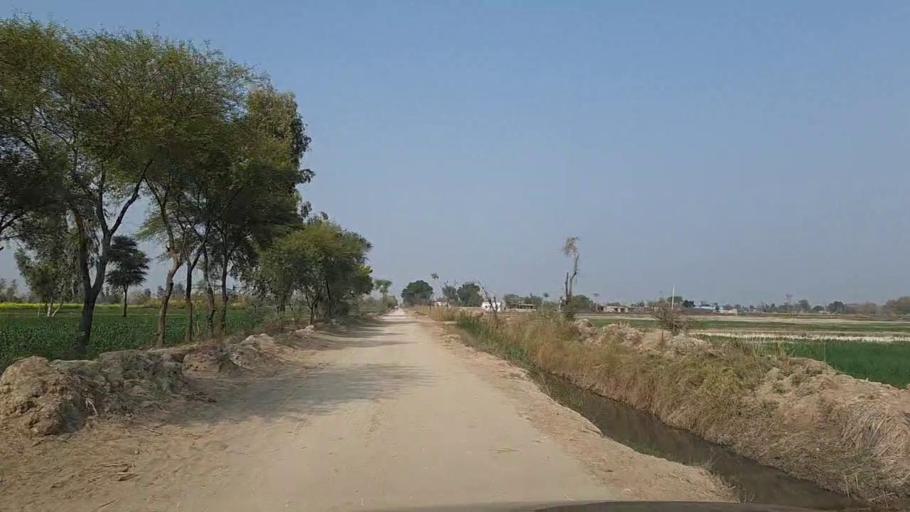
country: PK
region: Sindh
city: Daur
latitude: 26.3953
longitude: 68.4238
